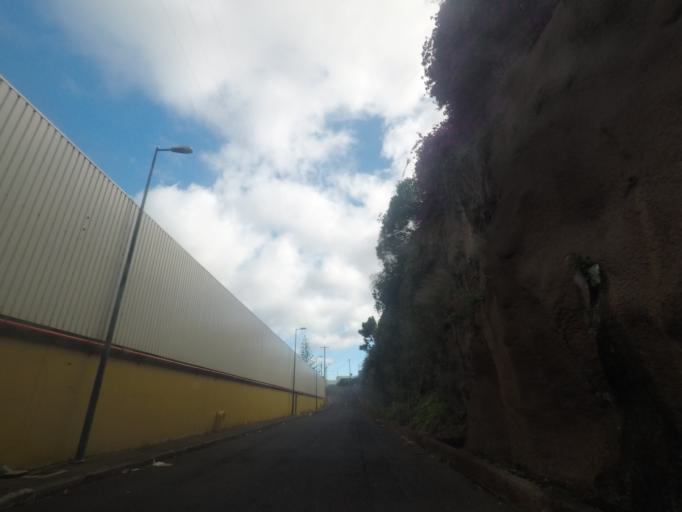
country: PT
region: Madeira
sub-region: Machico
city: Machico
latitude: 32.7026
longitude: -16.7750
